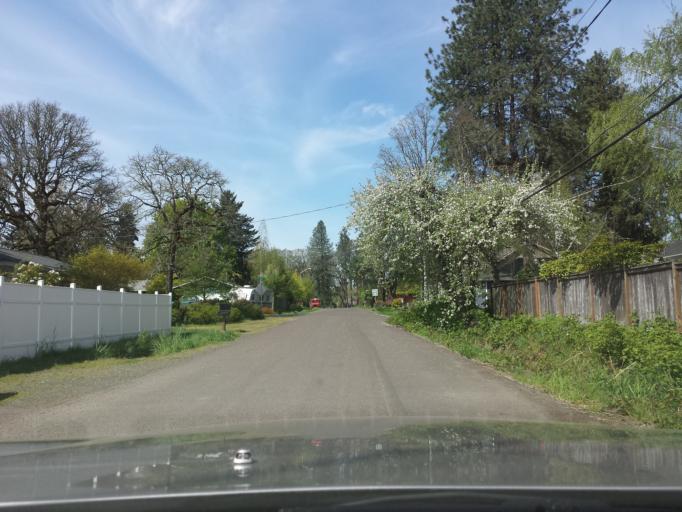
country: US
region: Oregon
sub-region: Washington County
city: Aloha
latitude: 45.4996
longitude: -122.8573
